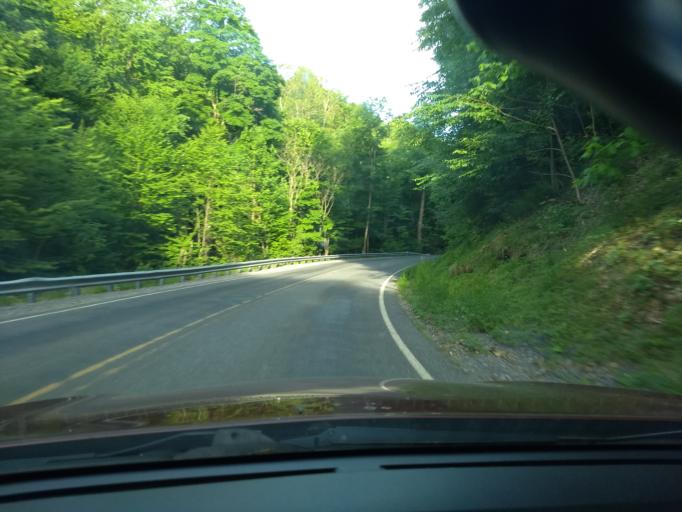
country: US
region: Pennsylvania
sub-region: Cambria County
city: Gallitzin
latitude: 40.5003
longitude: -78.5075
